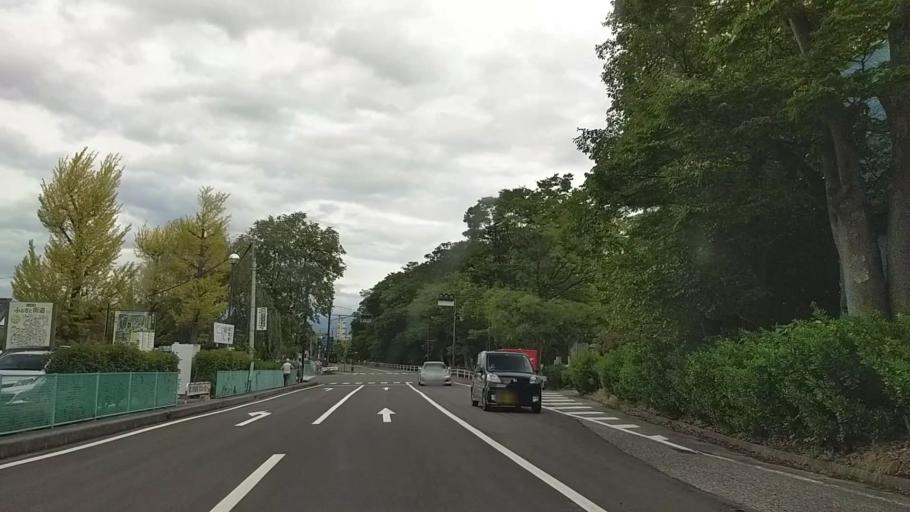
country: JP
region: Nagano
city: Nagano-shi
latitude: 36.6629
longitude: 138.1867
